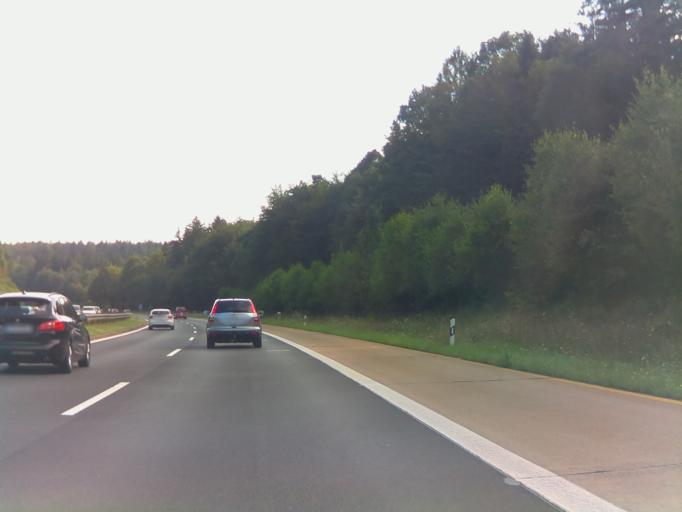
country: DE
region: Bavaria
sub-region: Regierungsbezirk Unterfranken
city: Schondra
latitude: 50.2478
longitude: 9.8744
